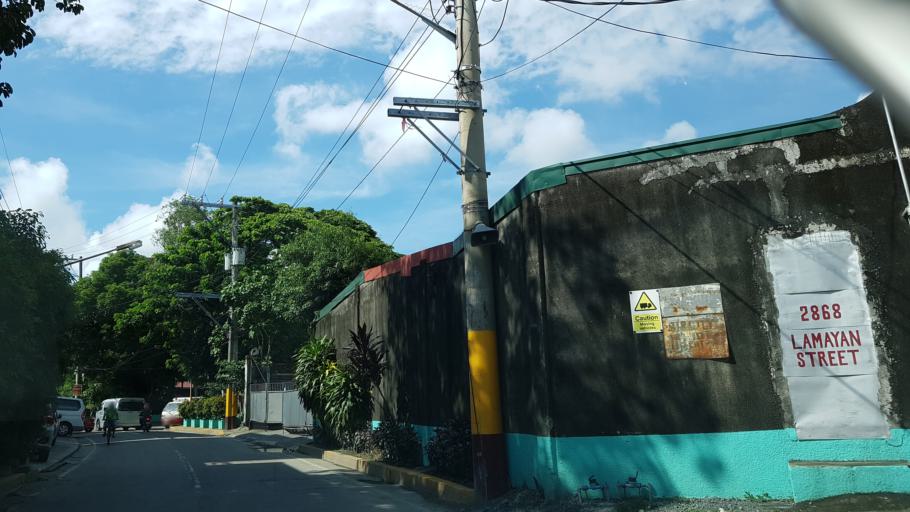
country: PH
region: Metro Manila
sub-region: San Juan
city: San Juan
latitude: 14.5838
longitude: 121.0182
